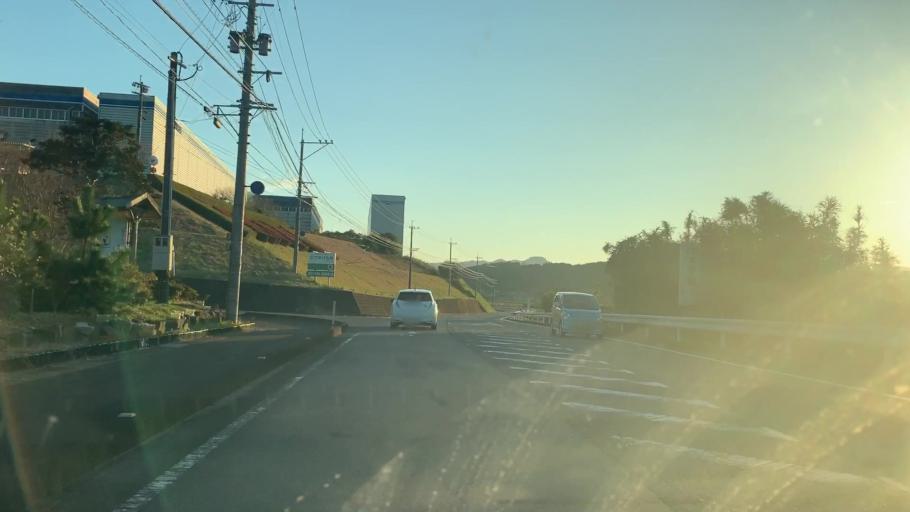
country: JP
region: Saga Prefecture
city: Imaricho-ko
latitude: 33.2801
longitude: 129.9667
